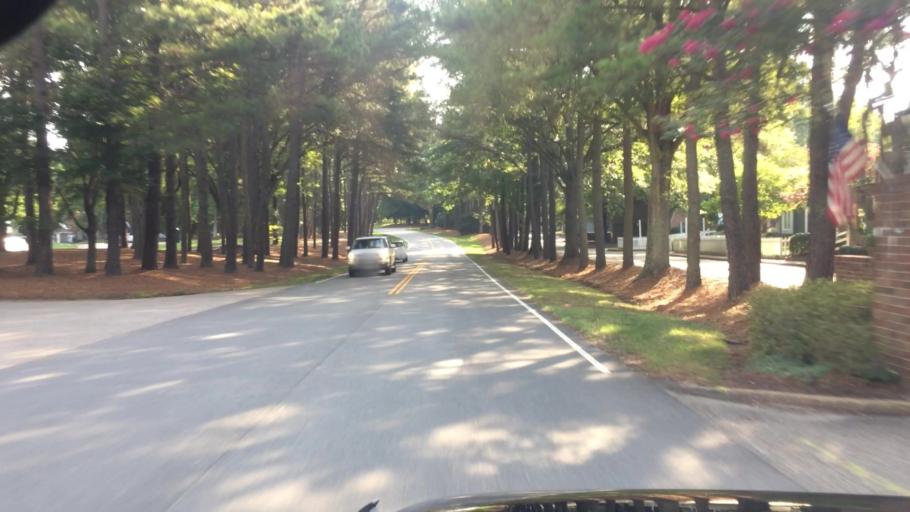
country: US
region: Virginia
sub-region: City of Williamsburg
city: Williamsburg
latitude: 37.2320
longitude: -76.6629
